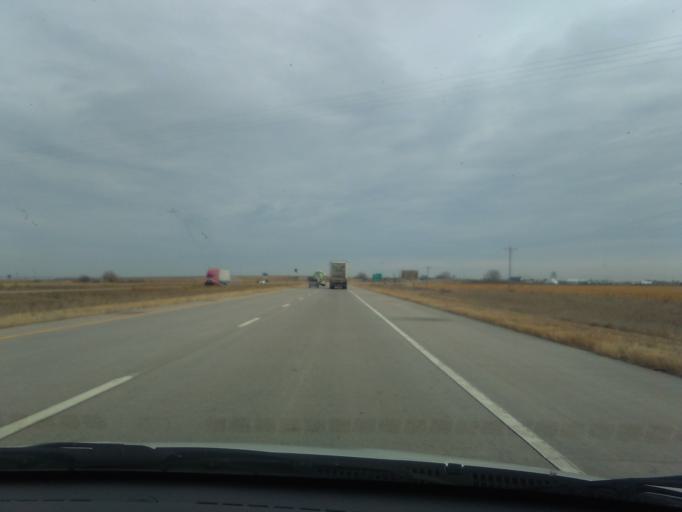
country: US
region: Colorado
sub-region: Morgan County
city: Fort Morgan
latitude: 40.2426
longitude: -104.0650
